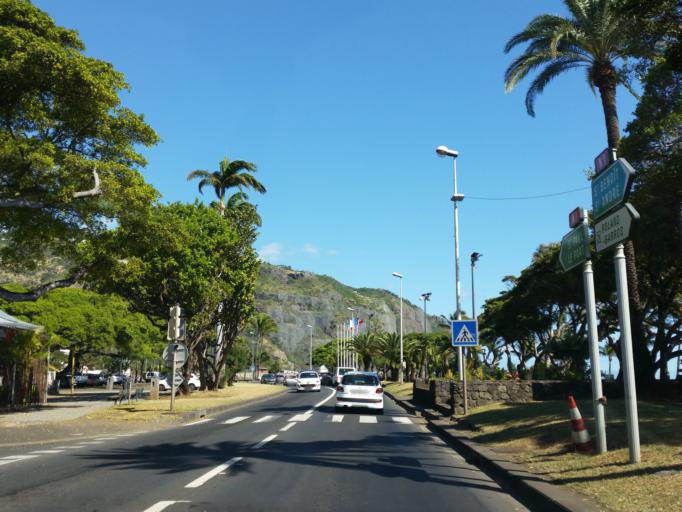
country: RE
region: Reunion
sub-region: Reunion
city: Saint-Denis
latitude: -20.8728
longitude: 55.4484
